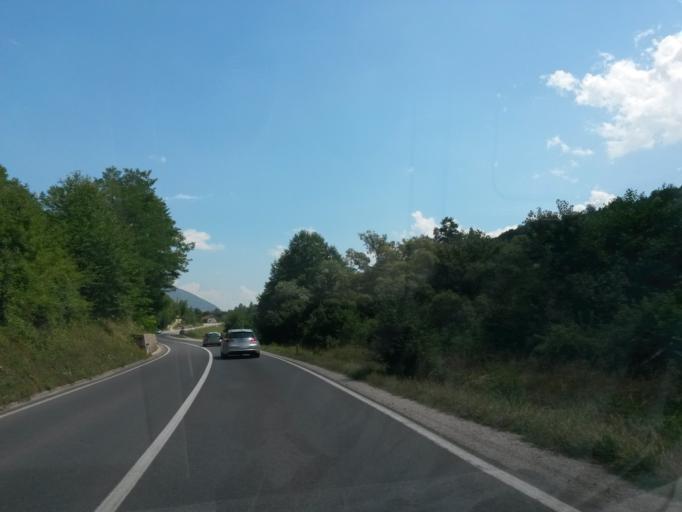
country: BA
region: Federation of Bosnia and Herzegovina
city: Travnik
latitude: 44.2321
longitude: 17.6203
